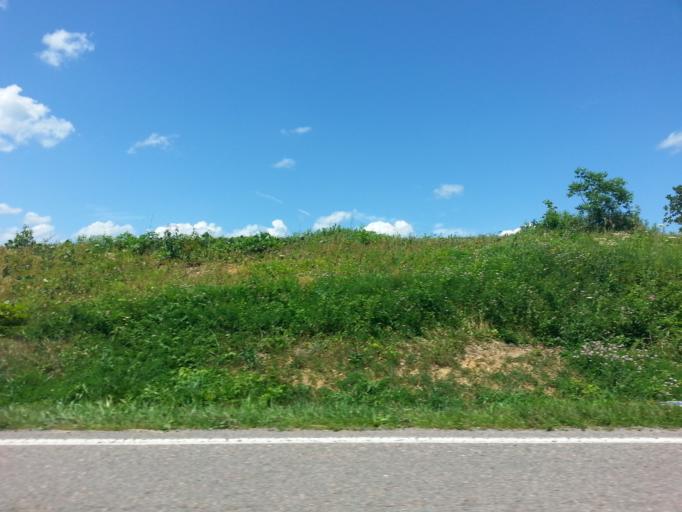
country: US
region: Virginia
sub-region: Lee County
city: Jonesville
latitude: 36.6962
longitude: -83.0610
